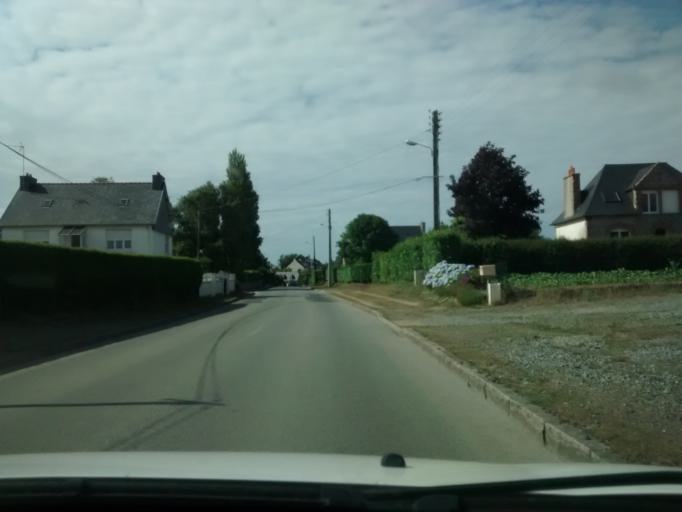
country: FR
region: Brittany
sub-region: Departement des Cotes-d'Armor
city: Penvenan
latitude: 48.8044
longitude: -3.2922
